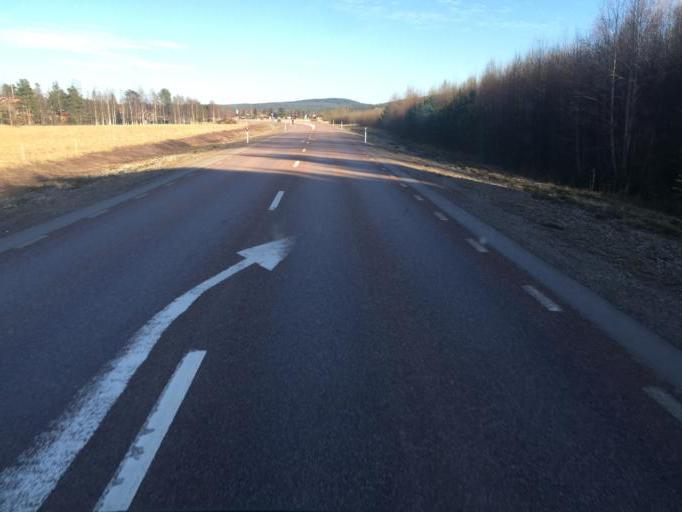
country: SE
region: Dalarna
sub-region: Gagnefs Kommun
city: Mockfjard
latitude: 60.4649
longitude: 14.6983
